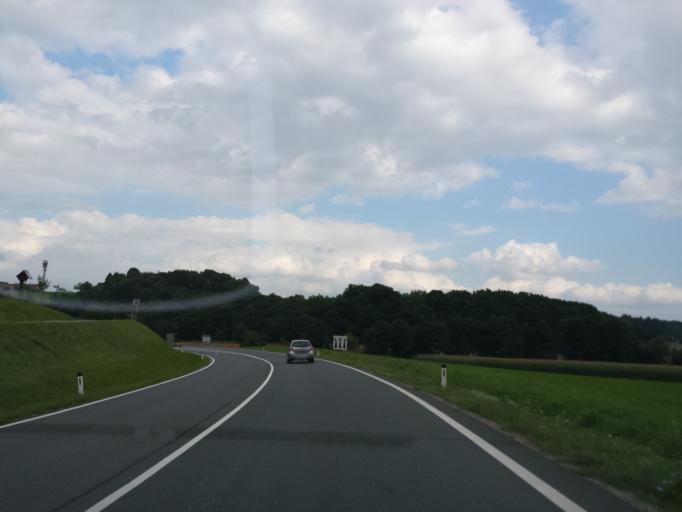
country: AT
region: Styria
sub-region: Politischer Bezirk Deutschlandsberg
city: Sankt Josef (Weststeiermark)
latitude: 46.9275
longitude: 15.3071
